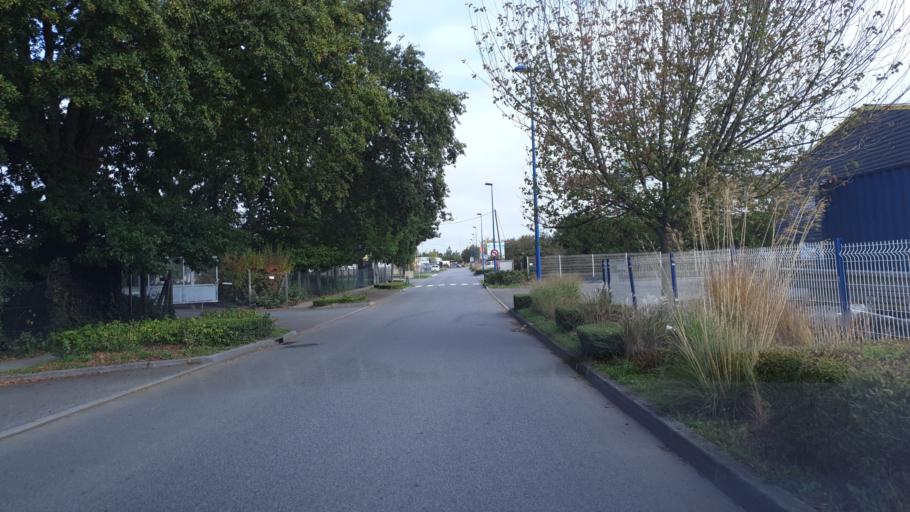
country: FR
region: Brittany
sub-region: Departement d'Ille-et-Vilaine
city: Janze
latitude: 47.9552
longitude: -1.4906
